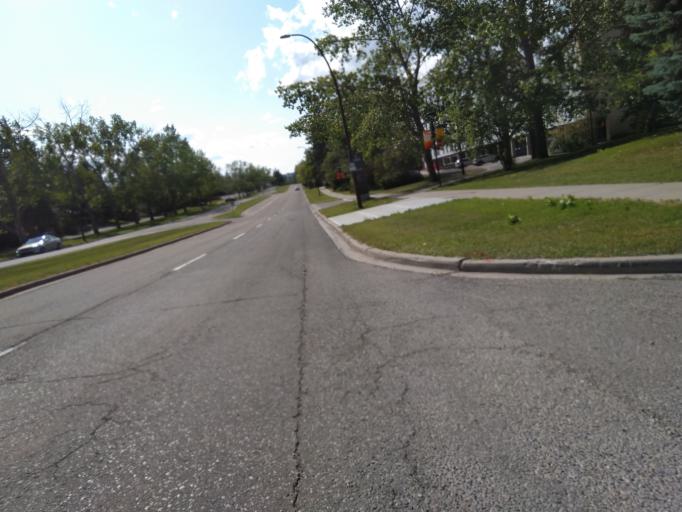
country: CA
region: Alberta
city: Calgary
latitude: 51.0745
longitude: -114.1357
